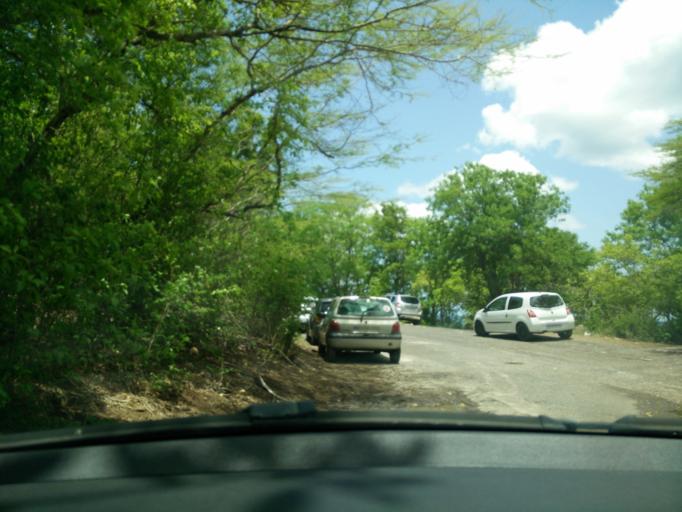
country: GP
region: Guadeloupe
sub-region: Guadeloupe
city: Sainte-Rose
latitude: 16.3502
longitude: -61.7701
